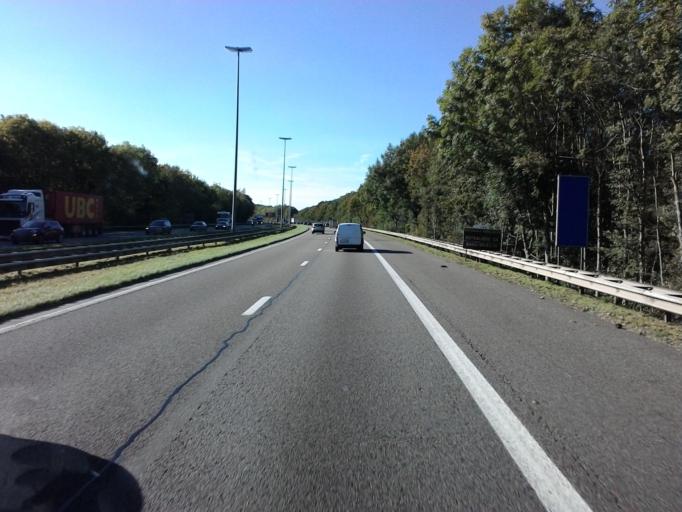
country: BE
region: Wallonia
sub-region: Province du Luxembourg
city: Arlon
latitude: 49.6664
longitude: 5.8062
